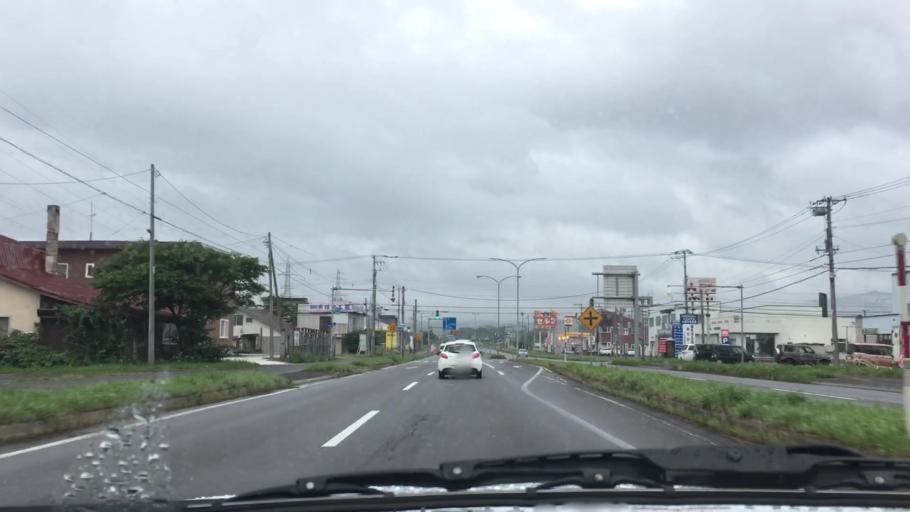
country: JP
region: Hokkaido
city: Nanae
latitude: 42.2496
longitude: 140.2864
